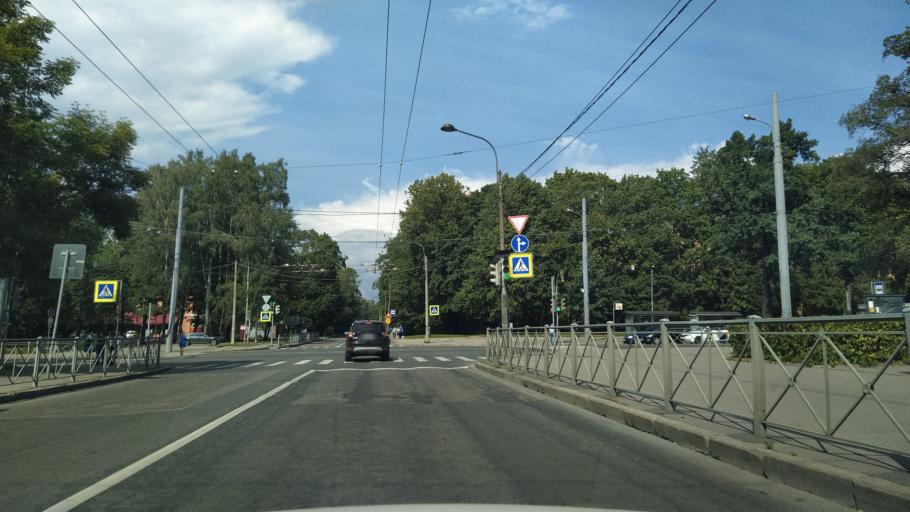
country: RU
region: Leningrad
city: Sampsonievskiy
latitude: 60.0001
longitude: 30.3478
